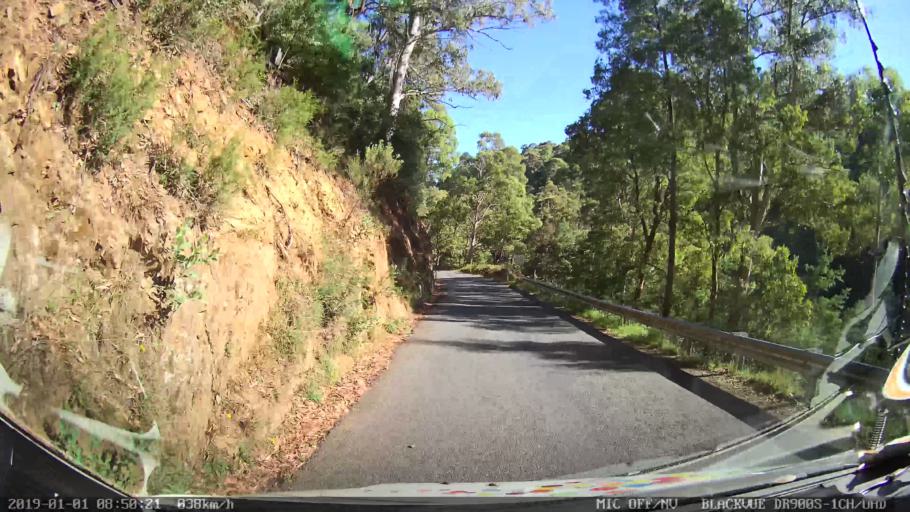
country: AU
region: New South Wales
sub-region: Snowy River
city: Jindabyne
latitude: -36.2769
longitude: 148.2028
